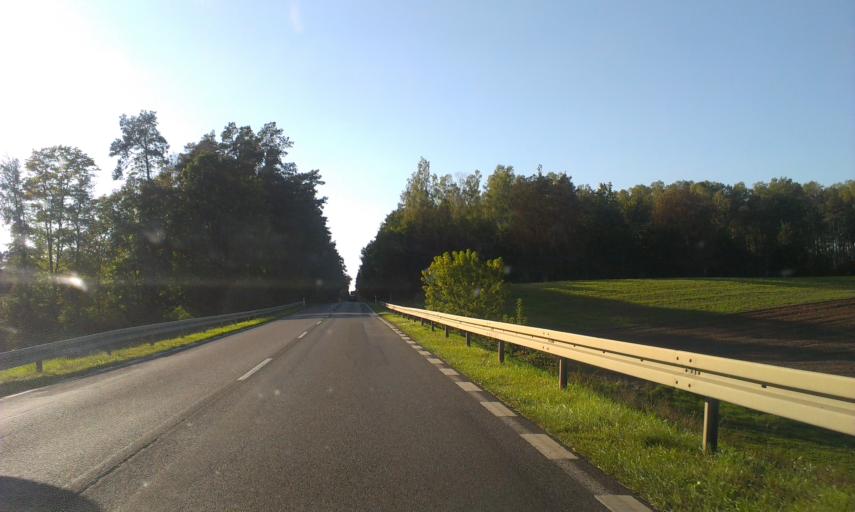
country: PL
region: Kujawsko-Pomorskie
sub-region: Powiat swiecki
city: Swiekatowo
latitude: 53.4859
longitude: 18.1226
